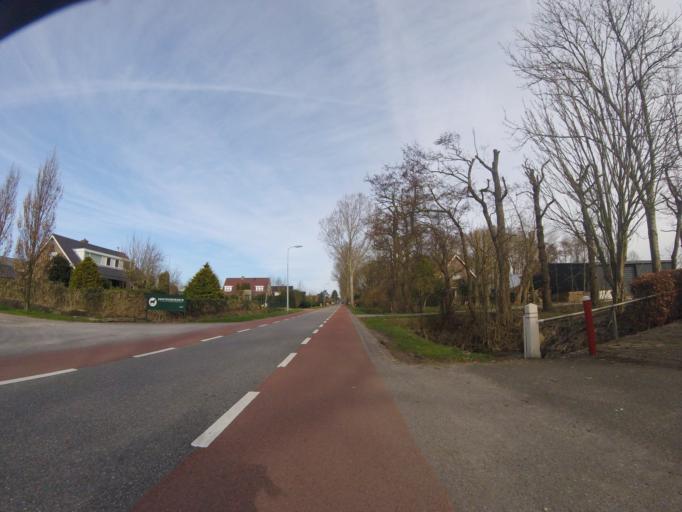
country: NL
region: North Holland
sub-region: Gemeente Bloemendaal
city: Bennebroek
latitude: 52.3035
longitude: 4.6106
